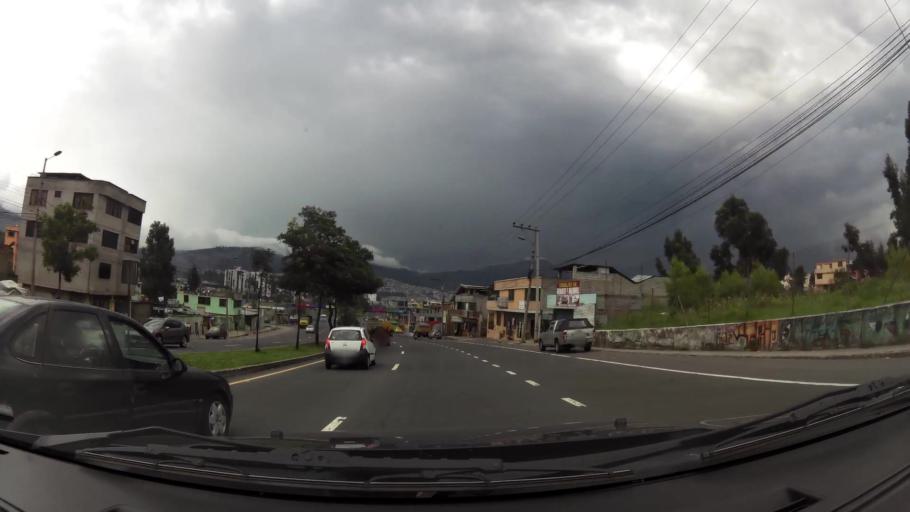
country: EC
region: Pichincha
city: Quito
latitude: -0.2918
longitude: -78.5356
